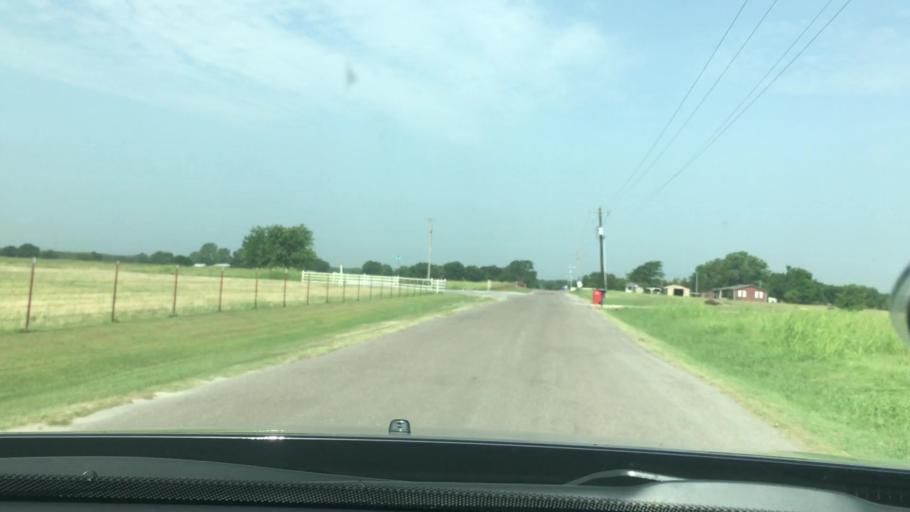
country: US
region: Oklahoma
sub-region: Garvin County
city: Pauls Valley
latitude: 34.7967
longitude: -97.1791
